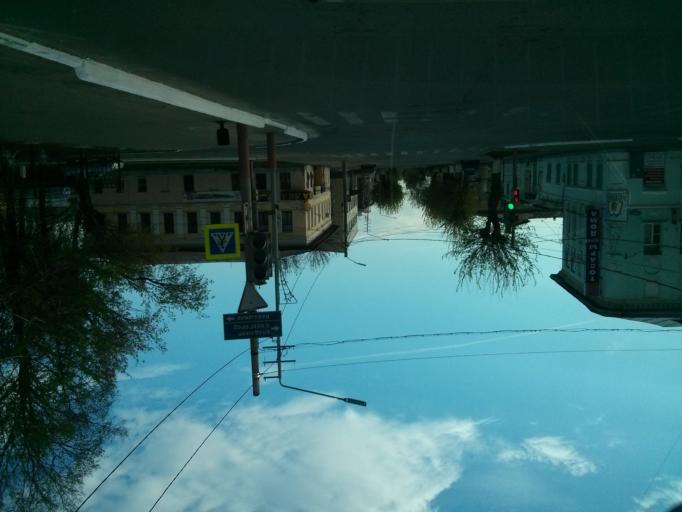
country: RU
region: Vladimir
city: Murom
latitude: 55.5800
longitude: 42.0517
